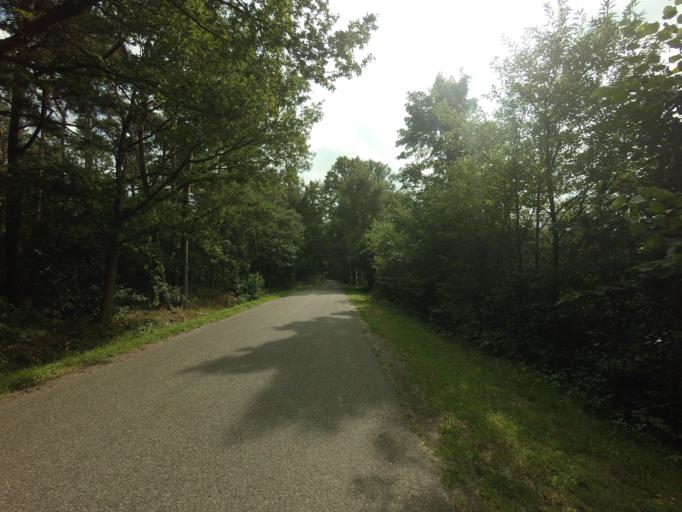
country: NL
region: Overijssel
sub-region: Gemeente Losser
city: Losser
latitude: 52.3151
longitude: 7.0303
